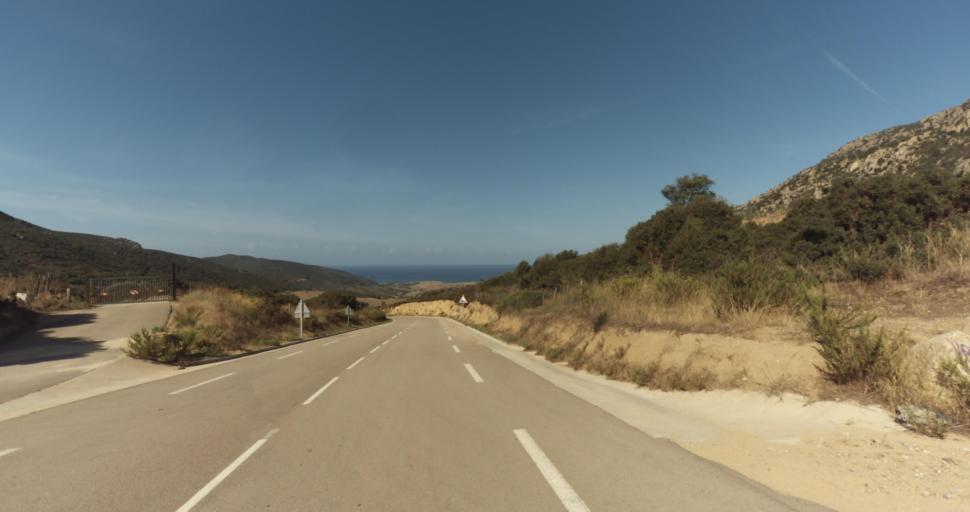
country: FR
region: Corsica
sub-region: Departement de la Corse-du-Sud
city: Ajaccio
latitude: 41.9329
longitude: 8.6782
